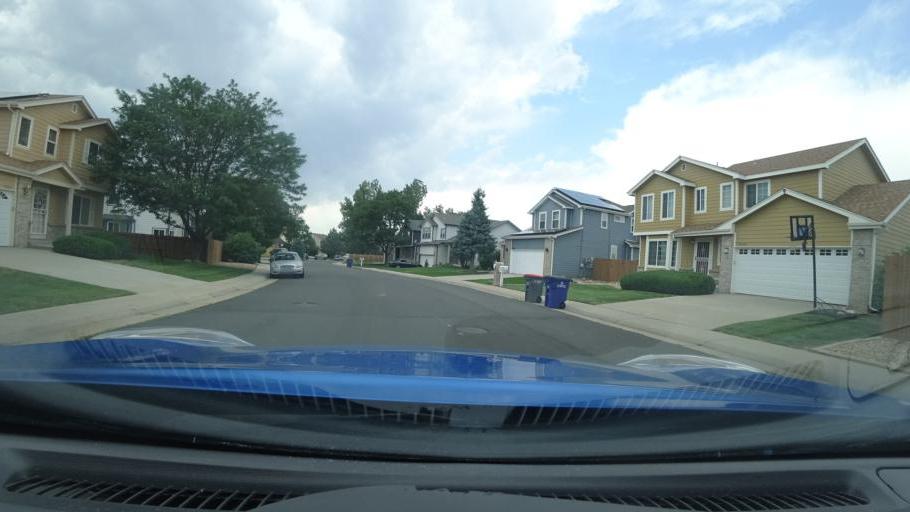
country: US
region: Colorado
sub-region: Adams County
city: Aurora
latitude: 39.6893
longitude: -104.7888
